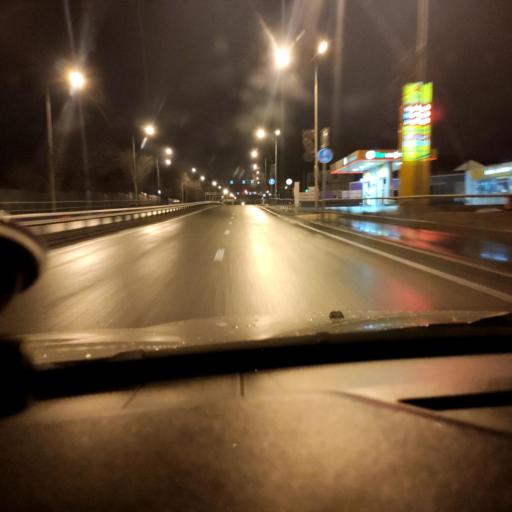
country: RU
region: Samara
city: Petra-Dubrava
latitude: 53.2984
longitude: 50.2445
